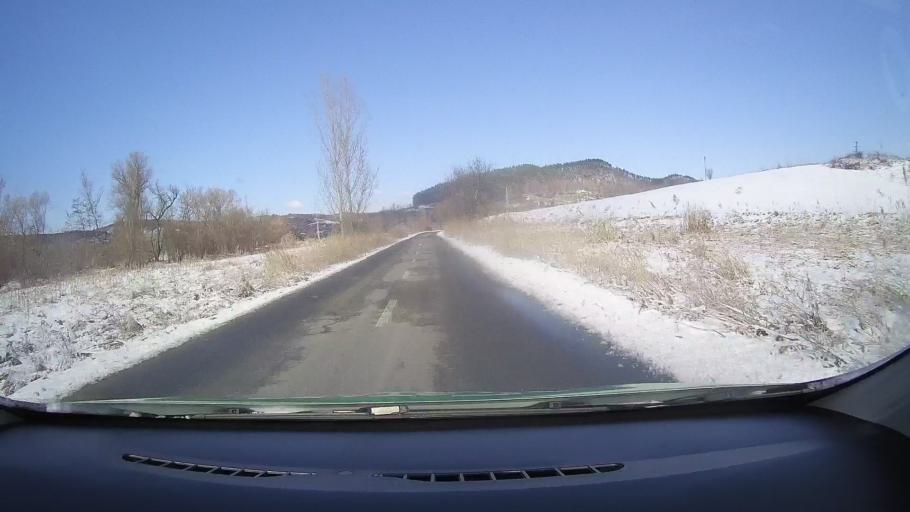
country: RO
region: Sibiu
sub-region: Comuna Mihaileni
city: Mihaileni
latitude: 46.0032
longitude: 24.3619
